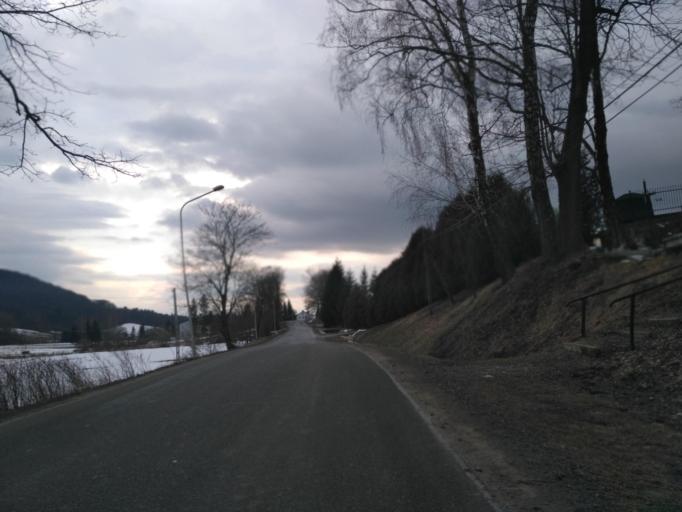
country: PL
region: Subcarpathian Voivodeship
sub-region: Powiat brzozowski
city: Dydnia
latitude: 49.6232
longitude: 22.1541
